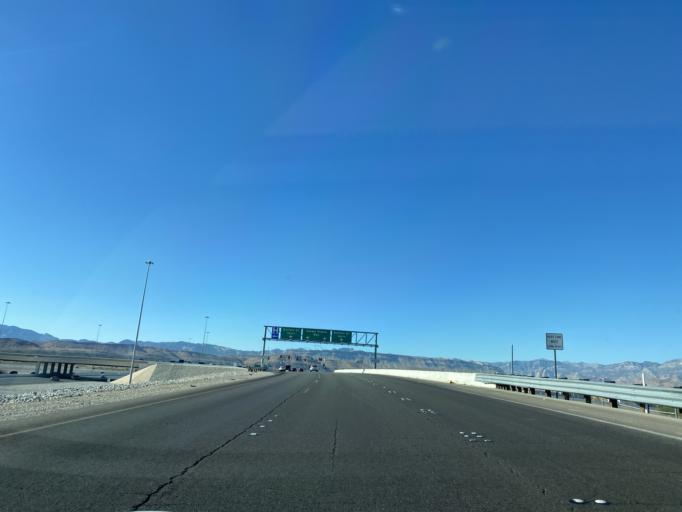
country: US
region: Nevada
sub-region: Clark County
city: Spring Valley
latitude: 36.0670
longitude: -115.2578
